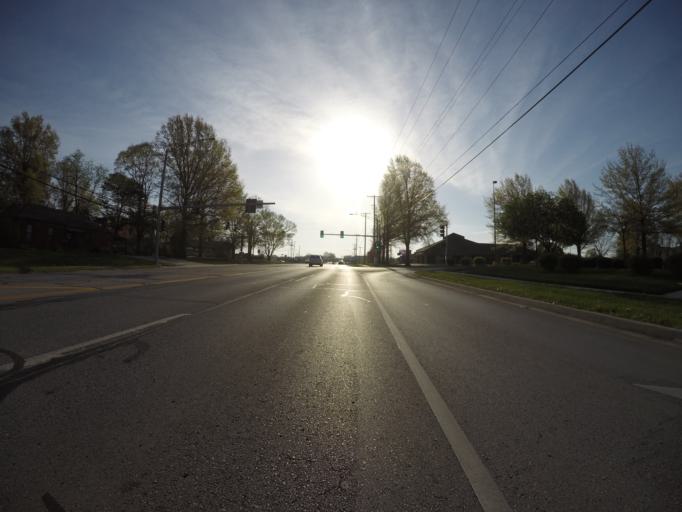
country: US
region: Missouri
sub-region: Jackson County
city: Lees Summit
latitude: 38.9113
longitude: -94.3984
